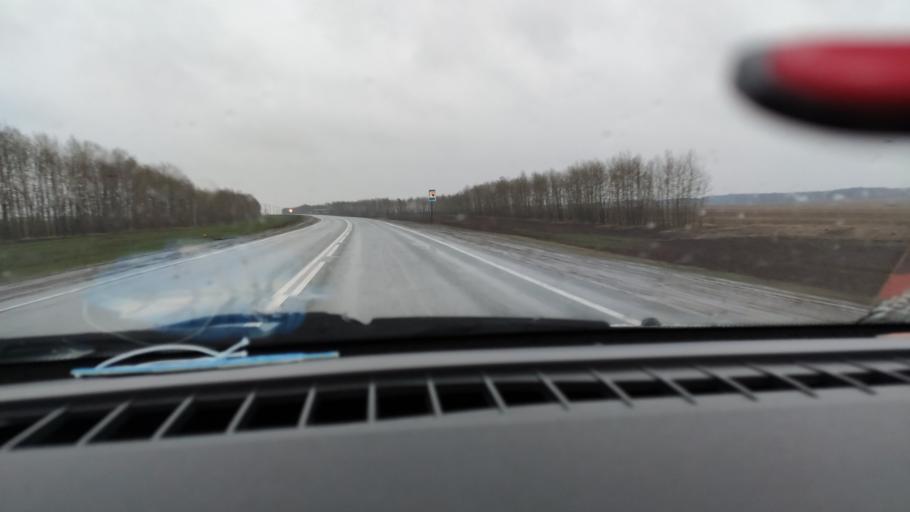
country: RU
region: Tatarstan
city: Mendeleyevsk
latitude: 55.9229
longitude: 52.2757
